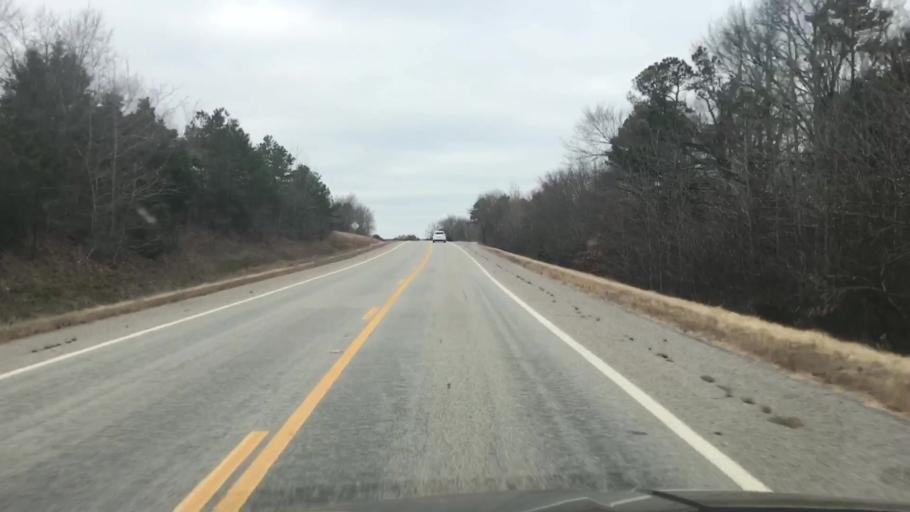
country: US
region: Arkansas
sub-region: Scott County
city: Waldron
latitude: 34.7018
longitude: -93.9178
